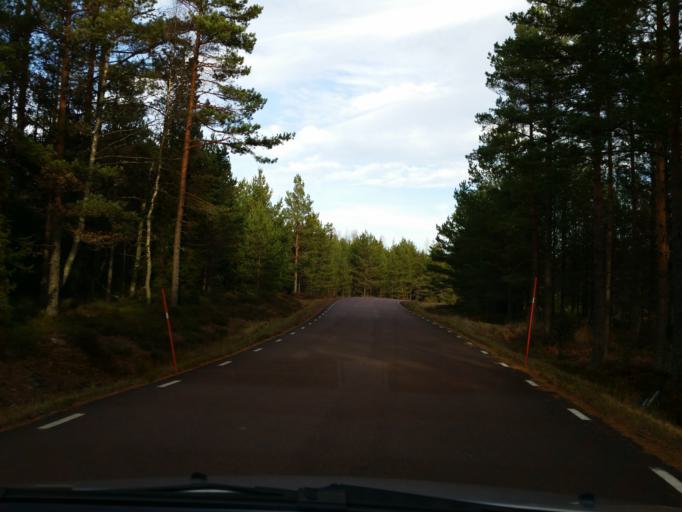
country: AX
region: Alands landsbygd
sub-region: Saltvik
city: Saltvik
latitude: 60.3335
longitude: 20.0877
